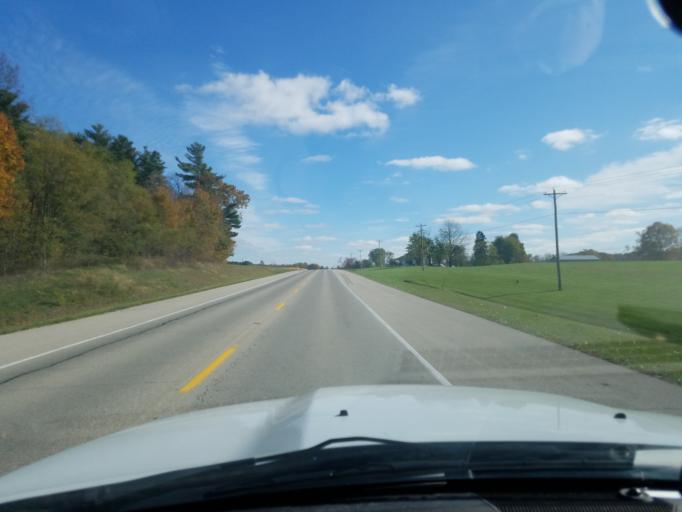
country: US
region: Indiana
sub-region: Ripley County
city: Osgood
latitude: 39.0750
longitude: -85.3237
